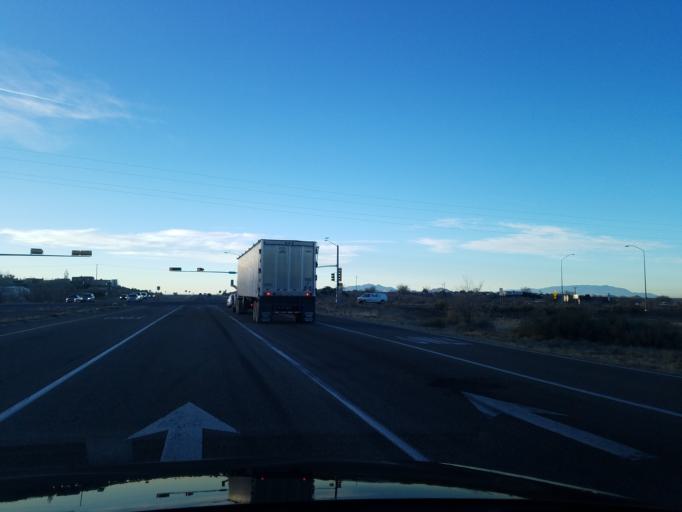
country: US
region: New Mexico
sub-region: Santa Fe County
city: Agua Fria
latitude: 35.6329
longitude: -106.0712
